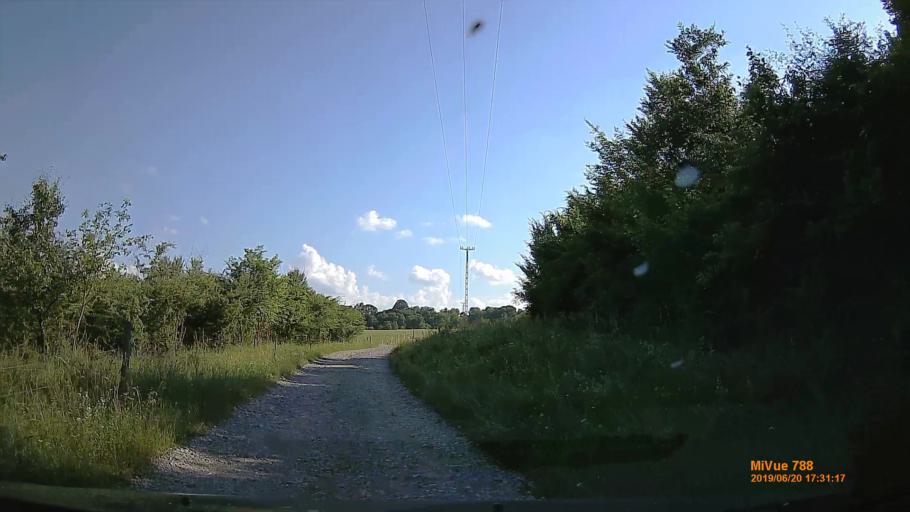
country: HU
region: Baranya
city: Buekkoesd
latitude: 46.1525
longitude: 18.0103
